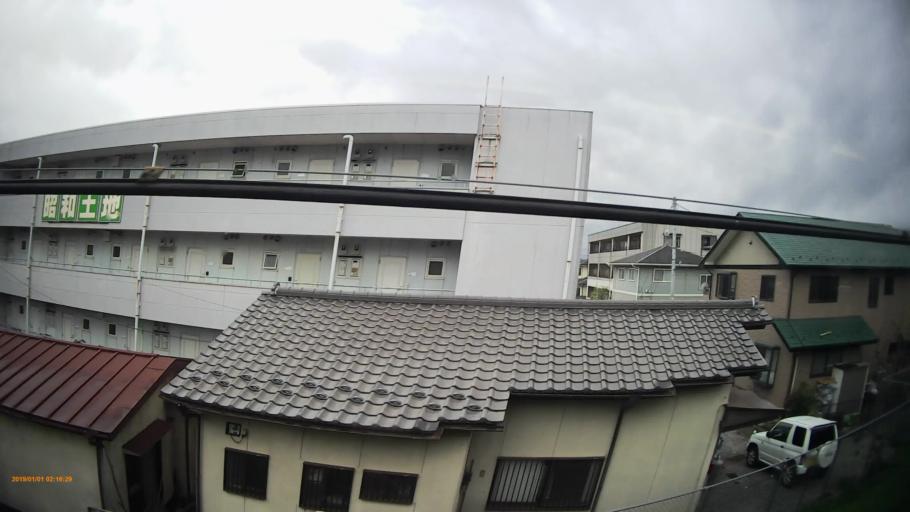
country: JP
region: Yamanashi
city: Kofu-shi
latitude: 35.6697
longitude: 138.5520
